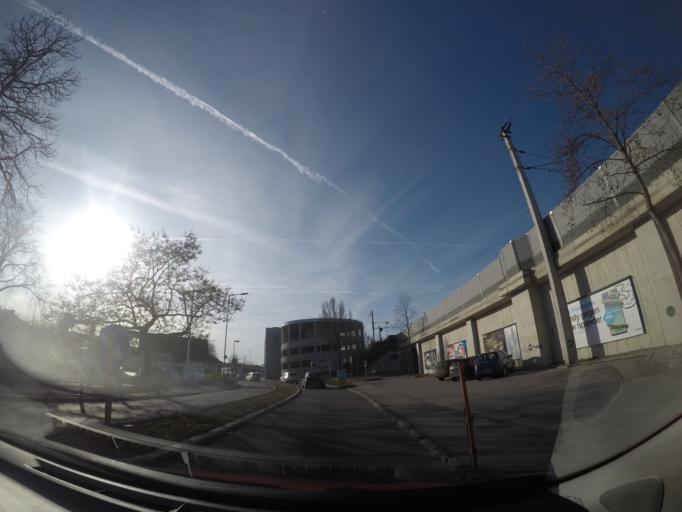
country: AT
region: Lower Austria
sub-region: Politischer Bezirk Baden
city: Baden
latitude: 48.0056
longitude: 16.2447
